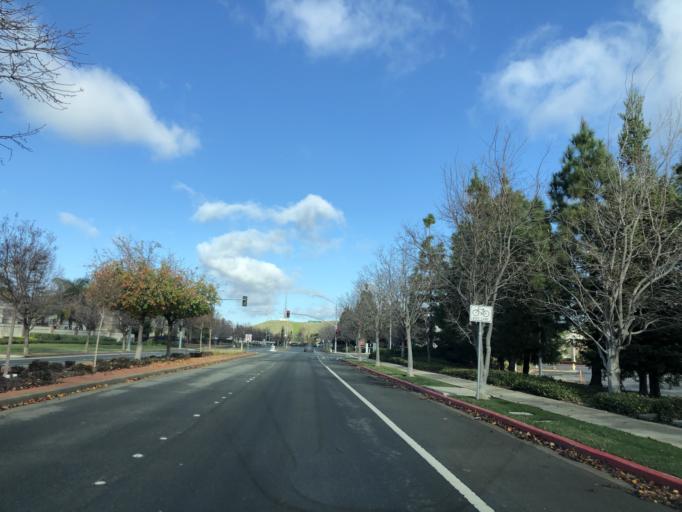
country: US
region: California
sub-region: Contra Costa County
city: Oakley
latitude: 37.9590
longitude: -121.7507
